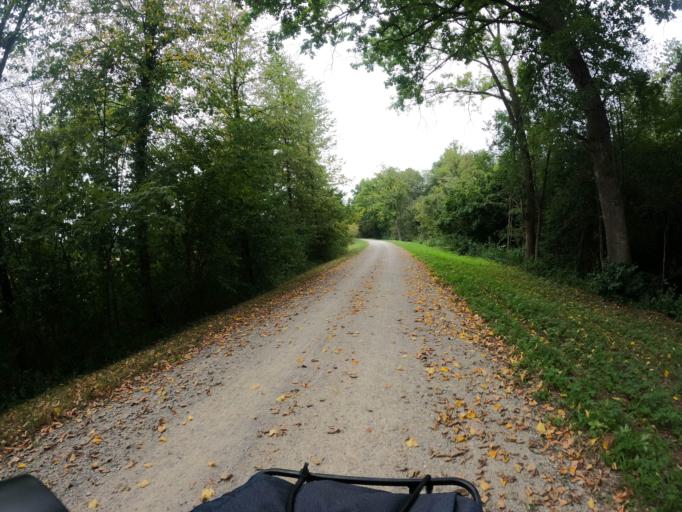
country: CH
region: Zurich
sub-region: Bezirk Affoltern
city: Ottenbach
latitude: 47.2710
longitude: 8.4001
